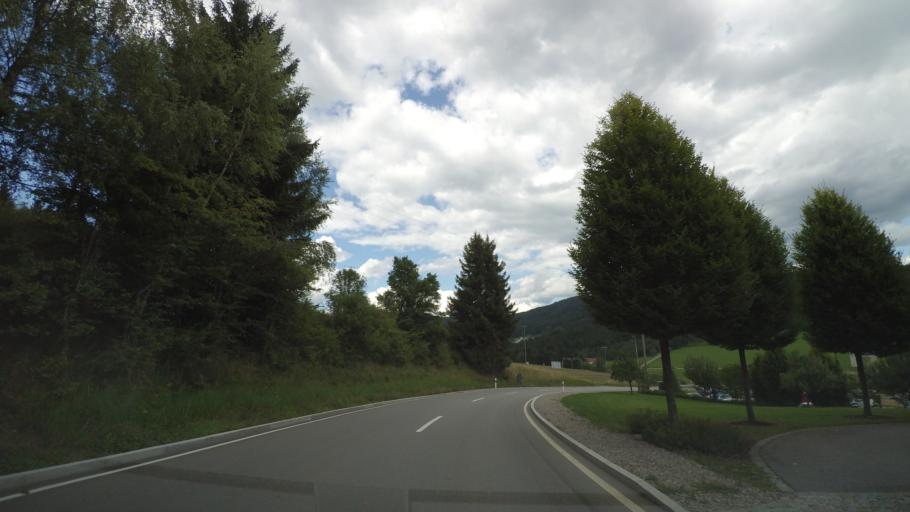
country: DE
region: Bavaria
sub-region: Lower Bavaria
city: Sankt Englmar
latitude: 49.0134
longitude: 12.7909
